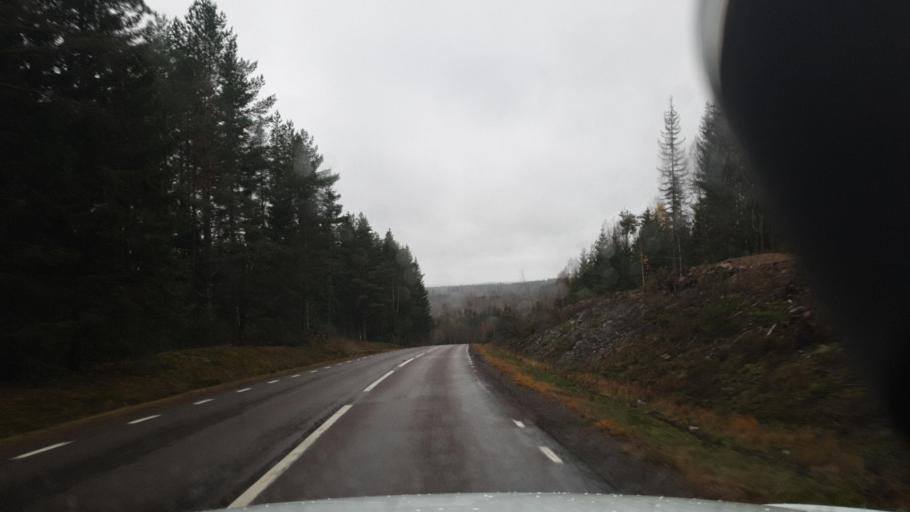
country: SE
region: Vaermland
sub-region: Sunne Kommun
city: Sunne
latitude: 59.6807
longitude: 13.0438
